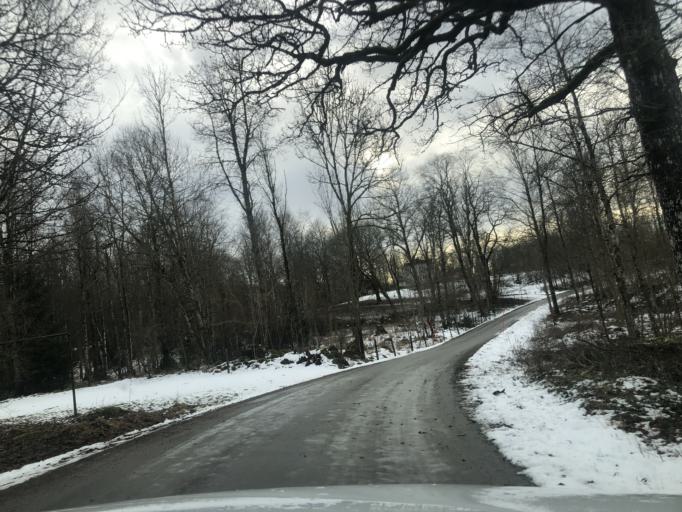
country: SE
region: Vaestra Goetaland
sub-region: Ulricehamns Kommun
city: Ulricehamn
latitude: 57.7696
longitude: 13.4703
